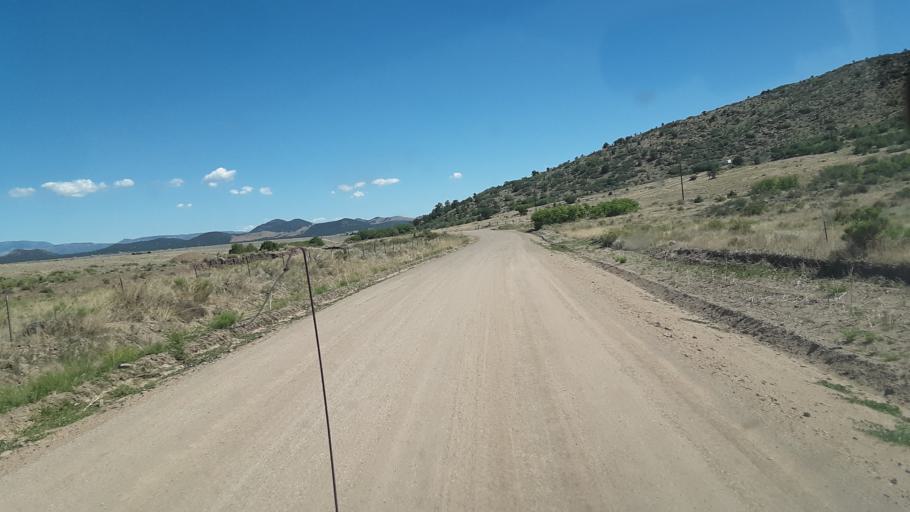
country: US
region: Colorado
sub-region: Custer County
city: Westcliffe
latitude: 38.2401
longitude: -105.5017
